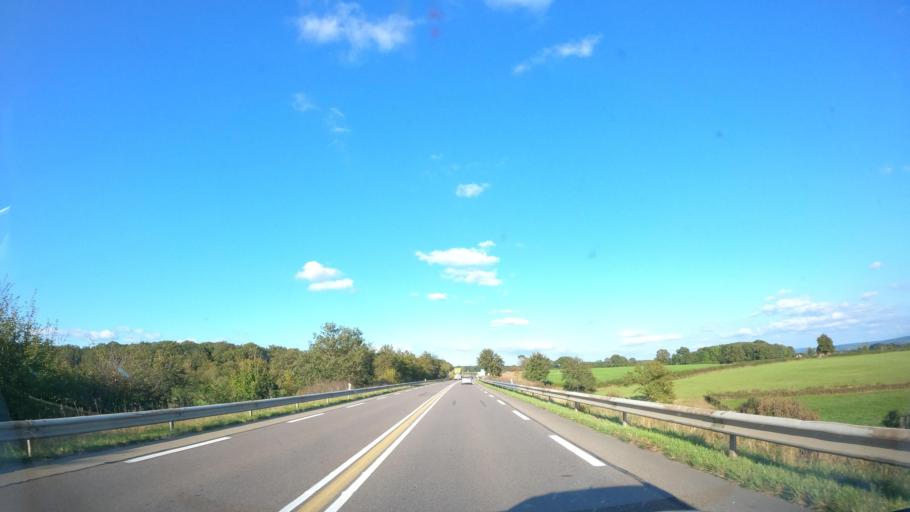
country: FR
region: Bourgogne
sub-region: Departement de Saone-et-Loire
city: Genelard
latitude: 46.6011
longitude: 4.2438
